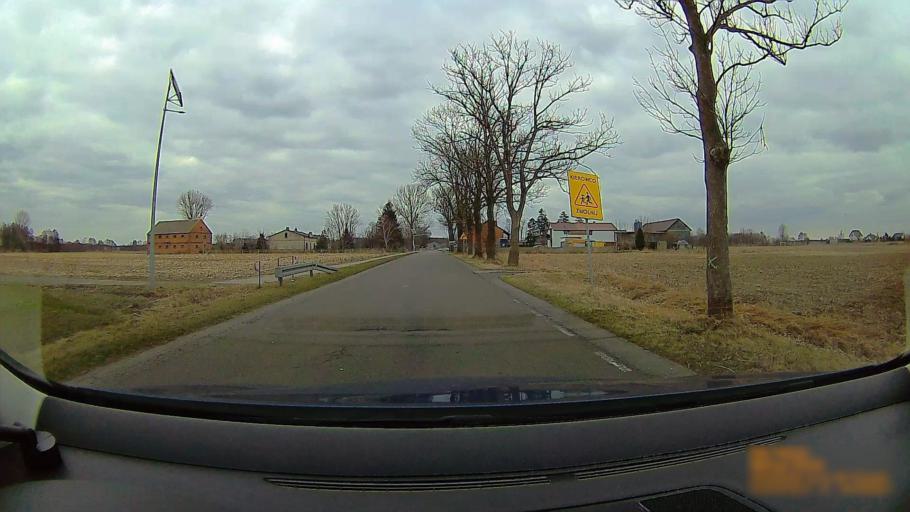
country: PL
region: Greater Poland Voivodeship
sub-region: Powiat koninski
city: Rzgow Pierwszy
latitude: 52.1256
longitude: 18.0610
